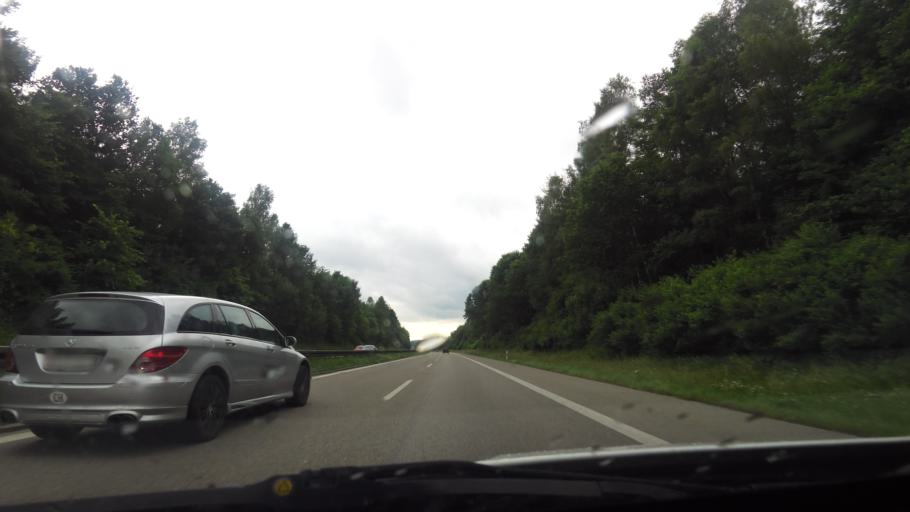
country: DE
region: Bavaria
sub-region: Swabia
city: Buxheim
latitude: 47.9822
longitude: 10.1266
